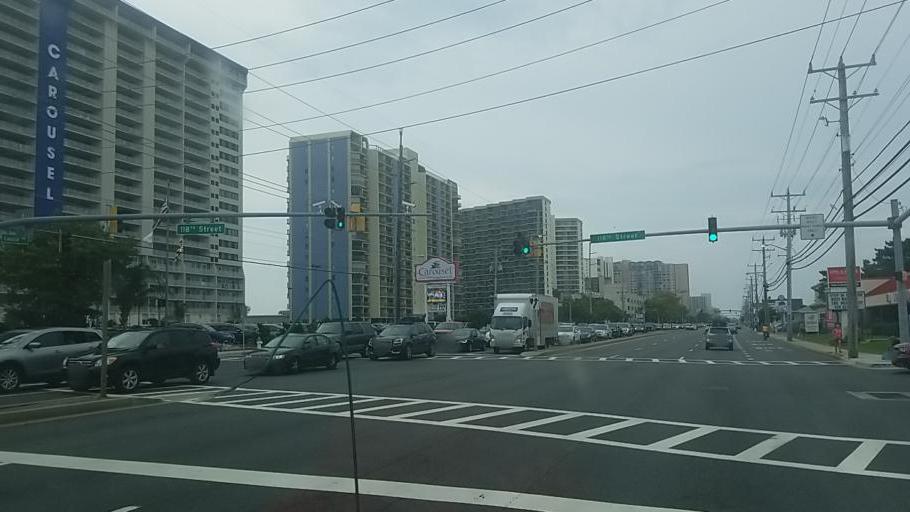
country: US
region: Maryland
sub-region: Worcester County
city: Ocean City
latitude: 38.4237
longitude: -75.0563
